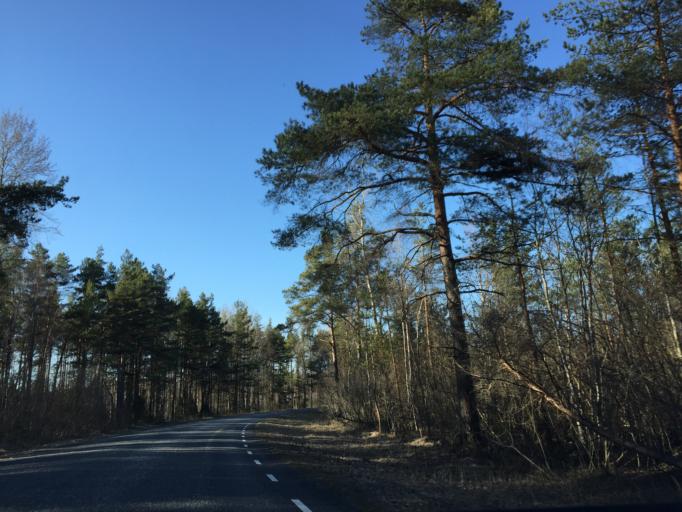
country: RU
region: Pskov
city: Gdov
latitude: 59.0112
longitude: 27.6821
